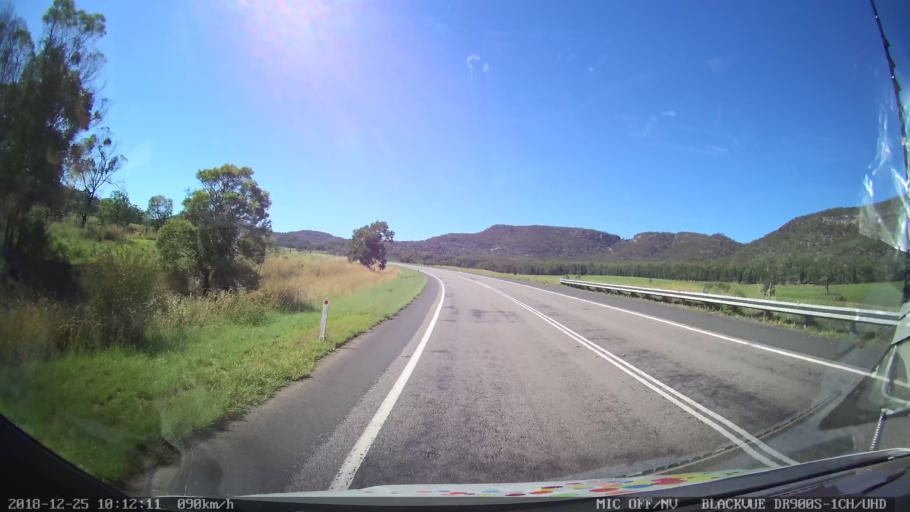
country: AU
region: New South Wales
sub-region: Muswellbrook
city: Denman
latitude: -32.3258
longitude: 150.5291
